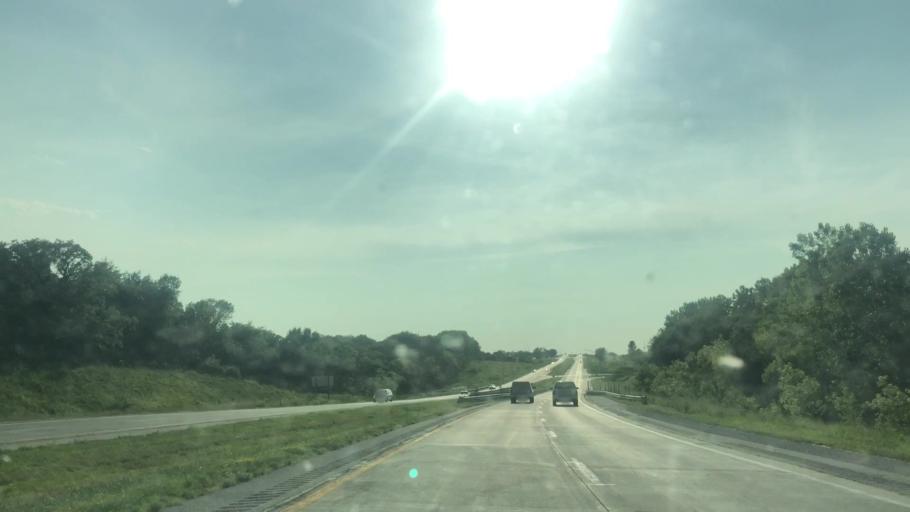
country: US
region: Iowa
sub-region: Story County
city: Nevada
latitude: 42.0055
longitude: -93.4481
